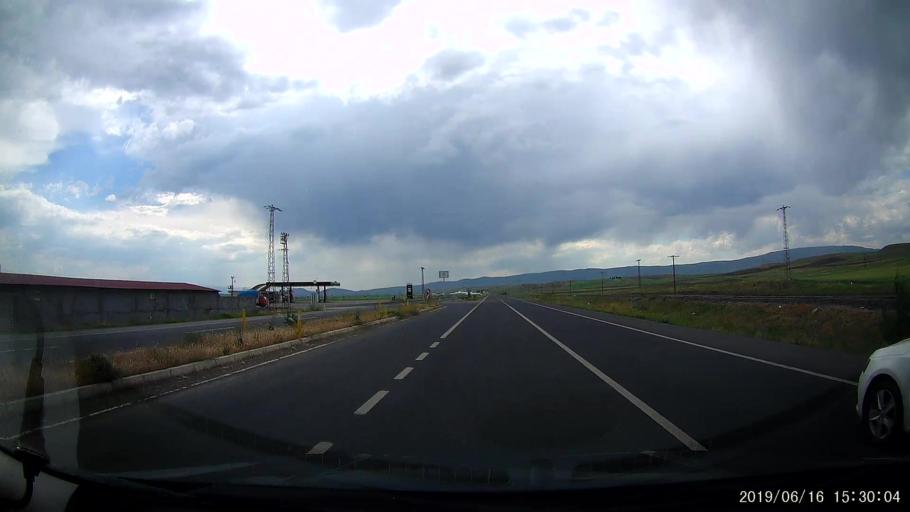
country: TR
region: Erzurum
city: Horasan
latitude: 40.0329
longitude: 42.1157
